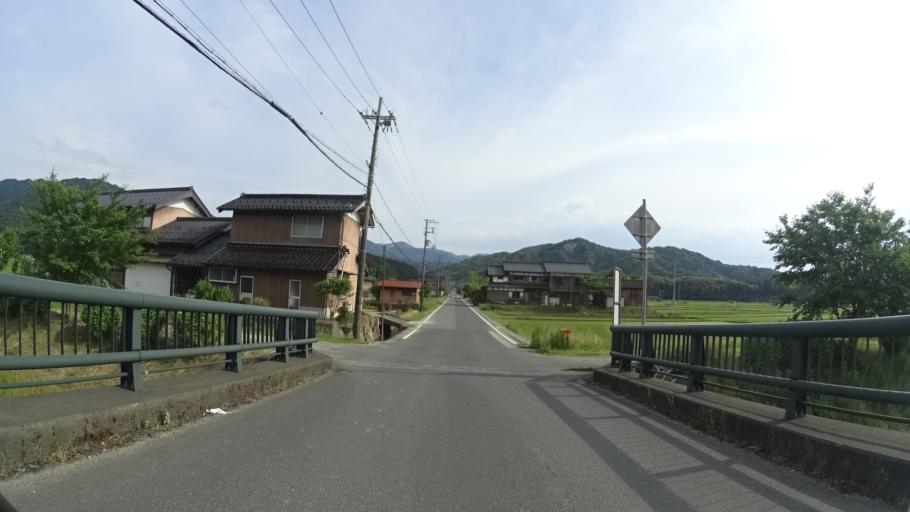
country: JP
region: Kyoto
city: Miyazu
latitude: 35.5288
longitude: 135.1272
